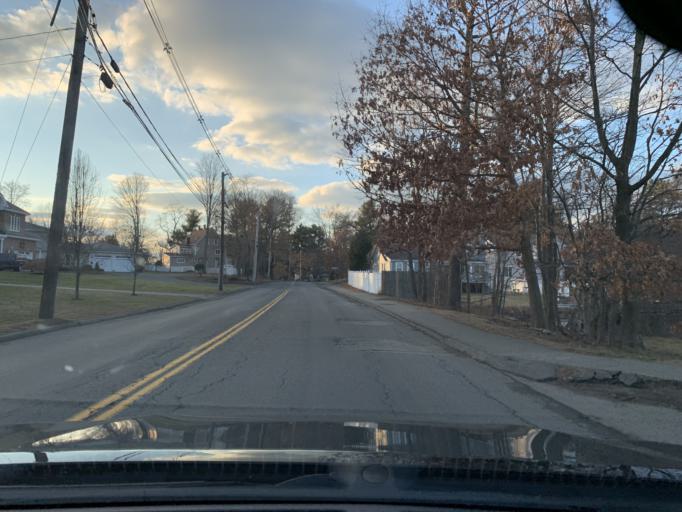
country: US
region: Massachusetts
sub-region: Essex County
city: Lynnfield
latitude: 42.5283
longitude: -71.0332
